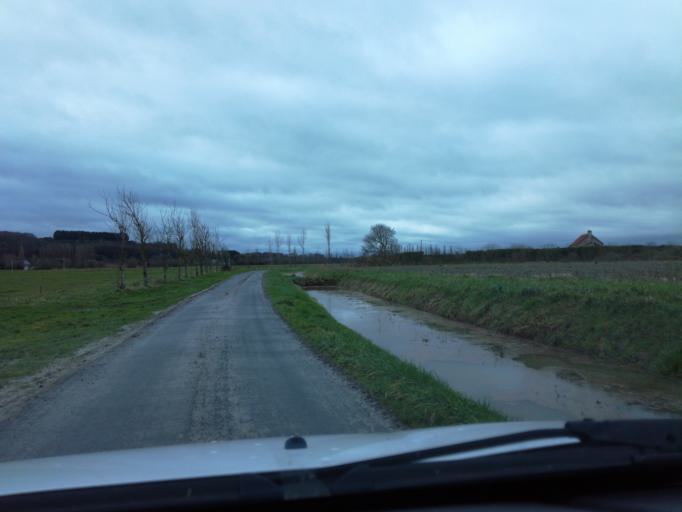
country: FR
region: Brittany
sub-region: Departement d'Ille-et-Vilaine
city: Cherrueix
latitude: 48.5804
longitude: -1.6933
